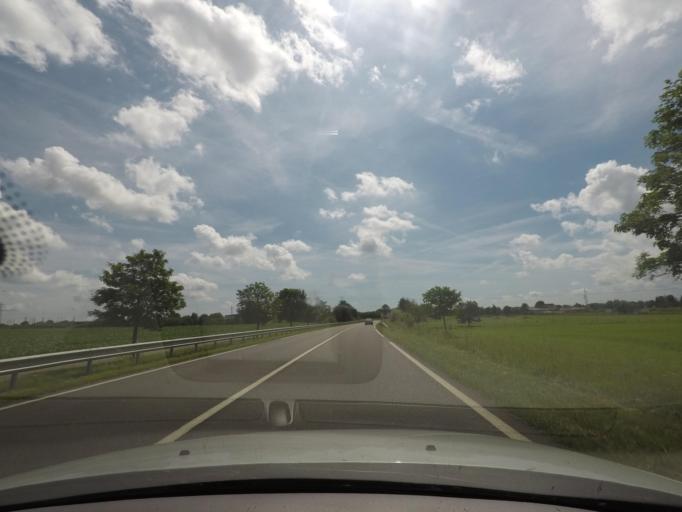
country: FR
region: Alsace
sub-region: Departement du Bas-Rhin
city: Drulingen
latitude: 48.8581
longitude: 7.1971
